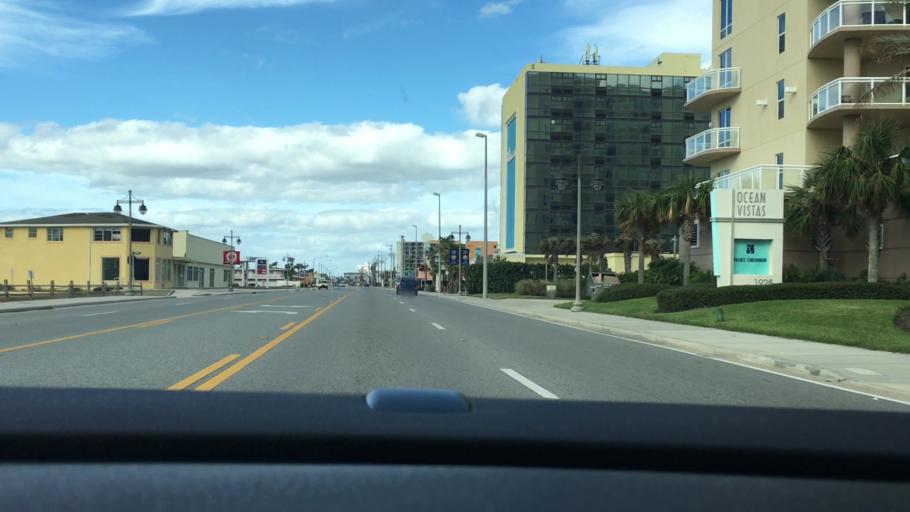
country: US
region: Florida
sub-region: Volusia County
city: Daytona Beach
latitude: 29.2035
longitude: -80.9967
